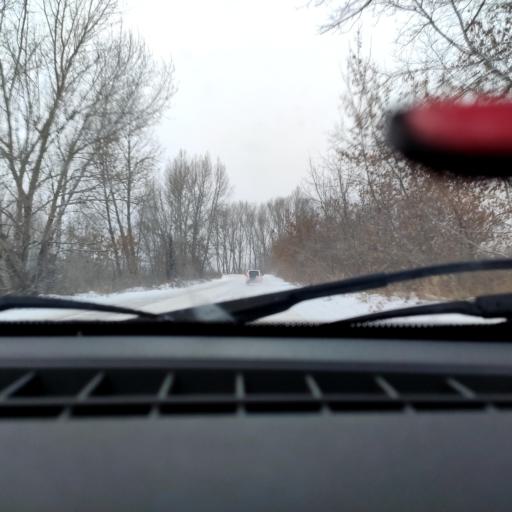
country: RU
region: Bashkortostan
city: Blagoveshchensk
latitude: 54.9091
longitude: 56.0070
